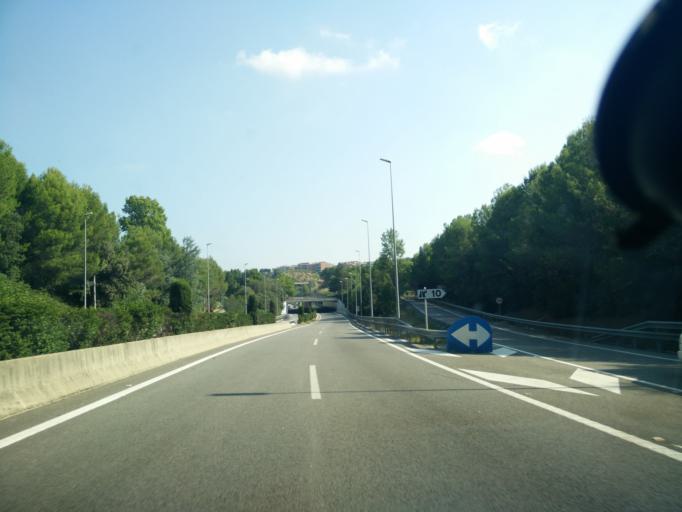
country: ES
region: Catalonia
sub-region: Provincia de Barcelona
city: Sant Cugat del Valles
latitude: 41.4665
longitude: 2.0640
